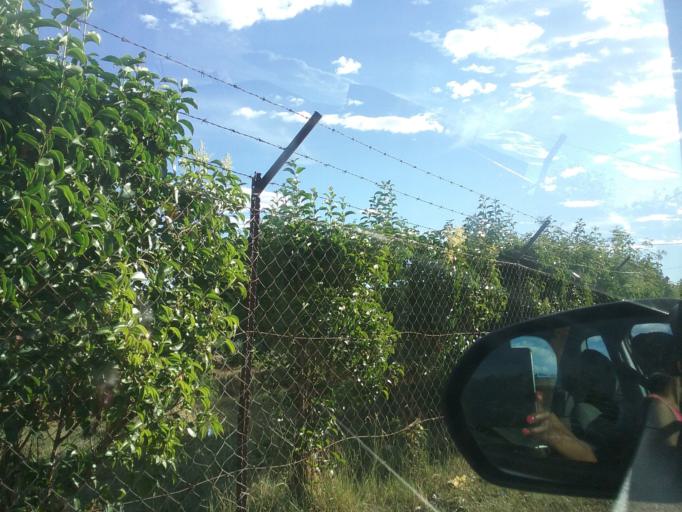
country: LS
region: Maseru
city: Maseru
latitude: -29.4314
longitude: 27.5712
